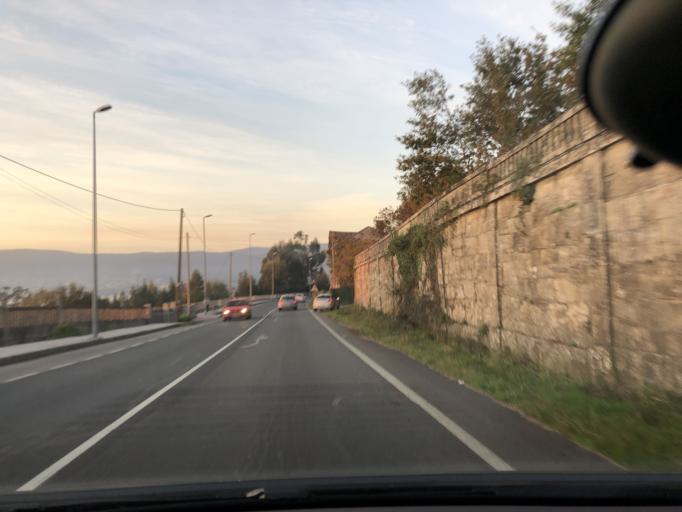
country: ES
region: Galicia
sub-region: Provincia de Pontevedra
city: Marin
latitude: 42.3903
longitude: -8.7125
